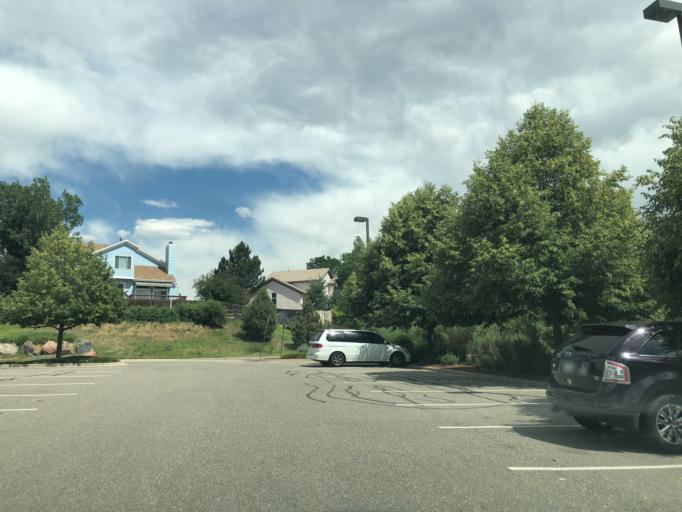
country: US
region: Colorado
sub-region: Arapahoe County
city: Dove Valley
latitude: 39.6171
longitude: -104.7678
